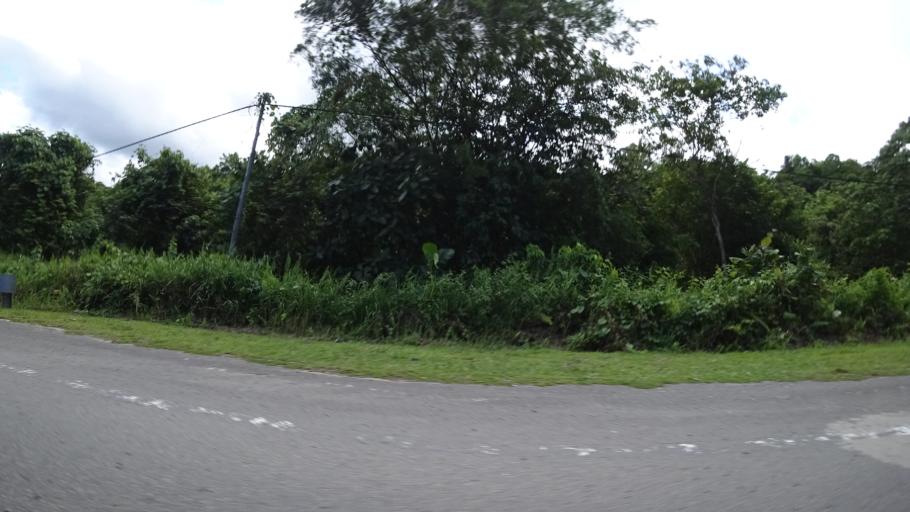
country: BN
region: Brunei and Muara
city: Bandar Seri Begawan
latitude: 4.8495
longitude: 114.9218
